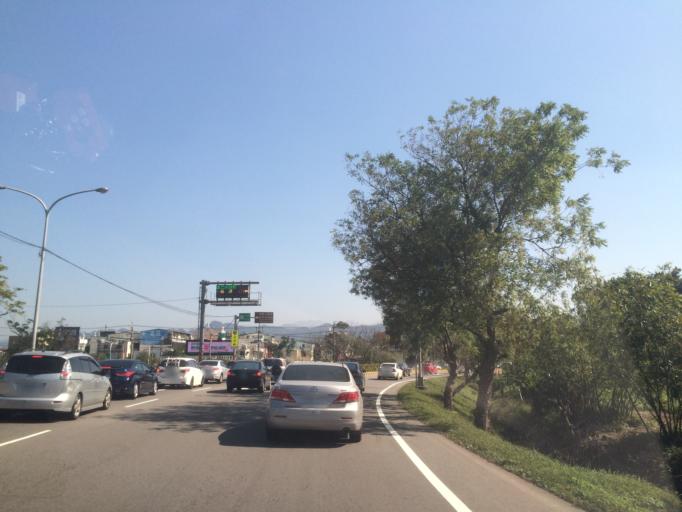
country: TW
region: Taiwan
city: Daxi
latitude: 24.8896
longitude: 121.2690
